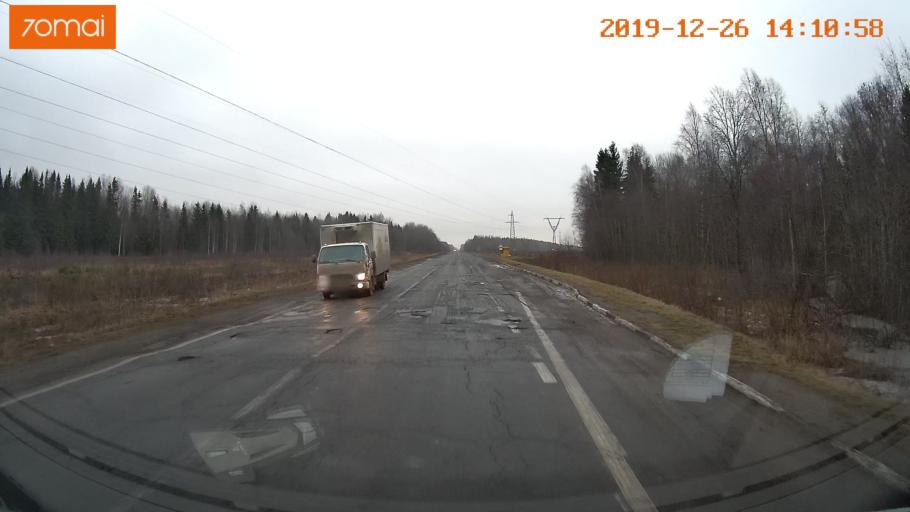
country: RU
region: Jaroslavl
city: Poshekhon'ye
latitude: 58.5089
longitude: 38.9645
